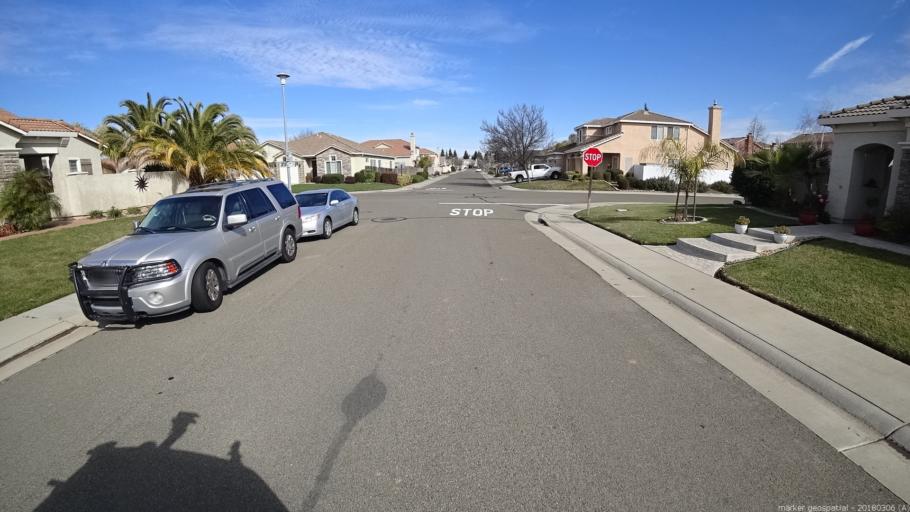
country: US
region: California
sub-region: Sacramento County
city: Vineyard
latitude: 38.4702
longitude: -121.3114
